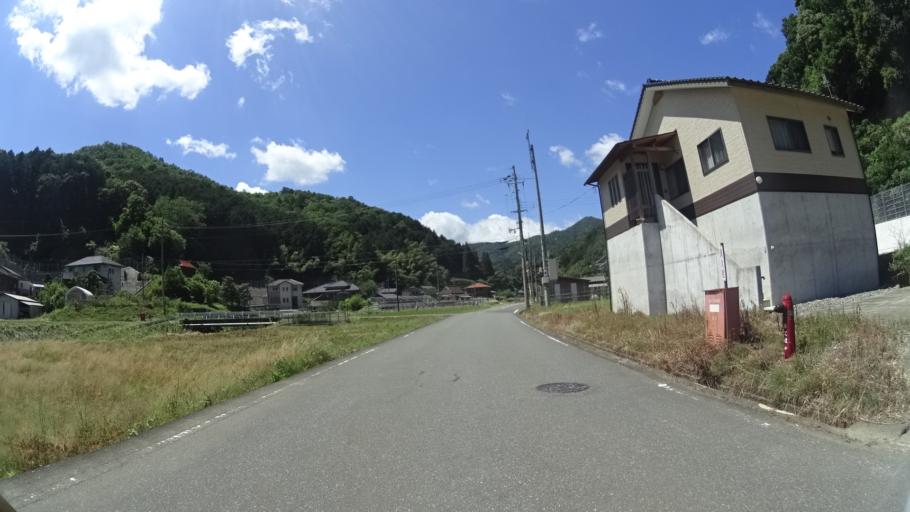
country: JP
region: Kyoto
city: Miyazu
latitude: 35.4117
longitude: 135.1896
